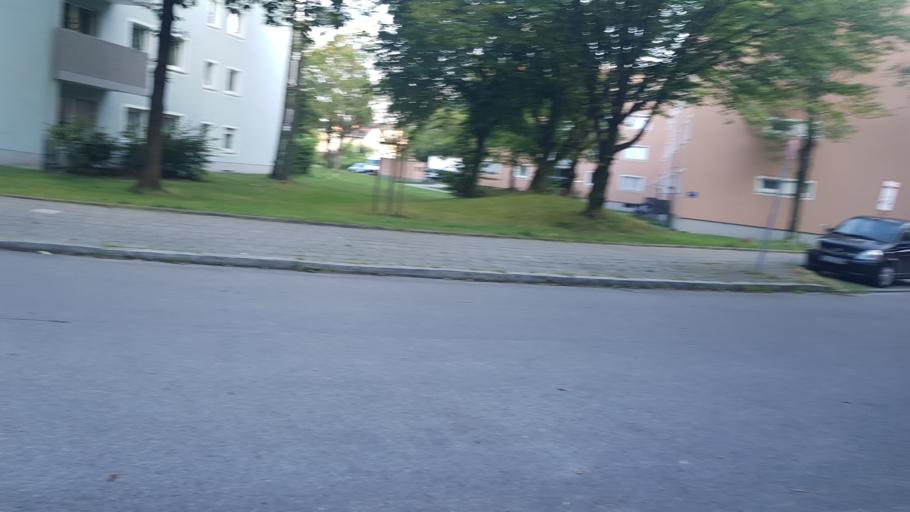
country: DE
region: Bavaria
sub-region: Upper Bavaria
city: Pasing
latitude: 48.1218
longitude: 11.4712
